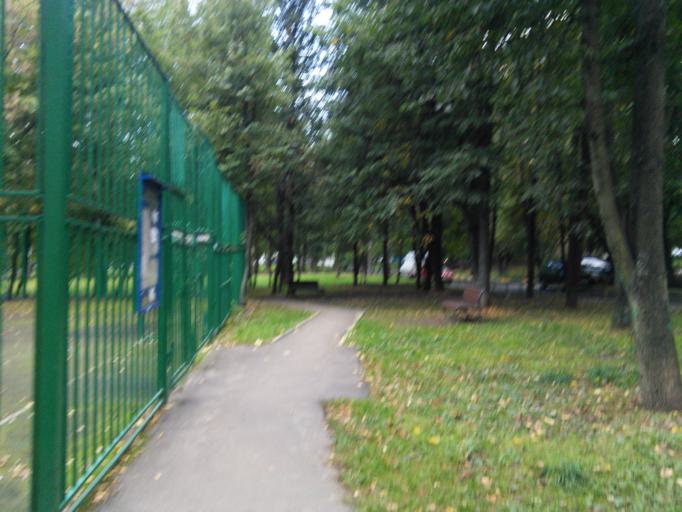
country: RU
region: Moskovskaya
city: Semenovskoye
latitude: 55.6898
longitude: 37.5558
